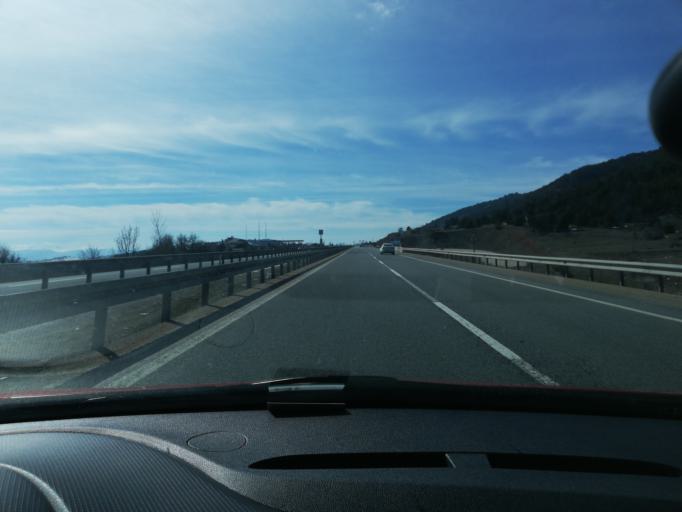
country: TR
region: Bolu
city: Gerede
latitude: 40.8212
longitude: 32.3193
